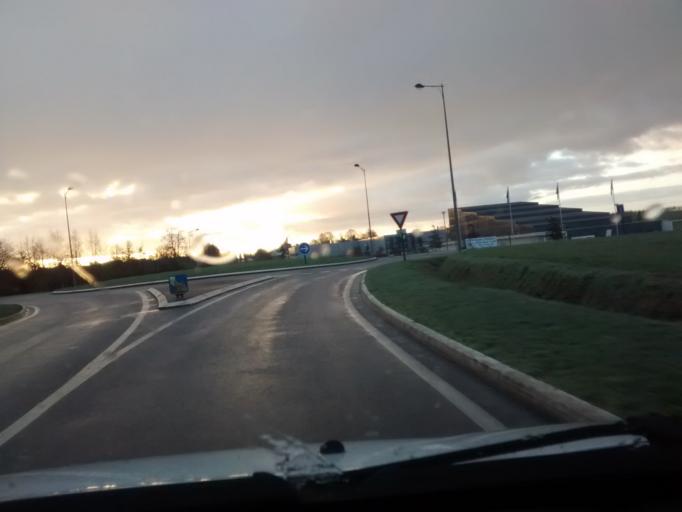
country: FR
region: Brittany
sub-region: Departement d'Ille-et-Vilaine
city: Bais
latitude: 48.0183
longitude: -1.3020
